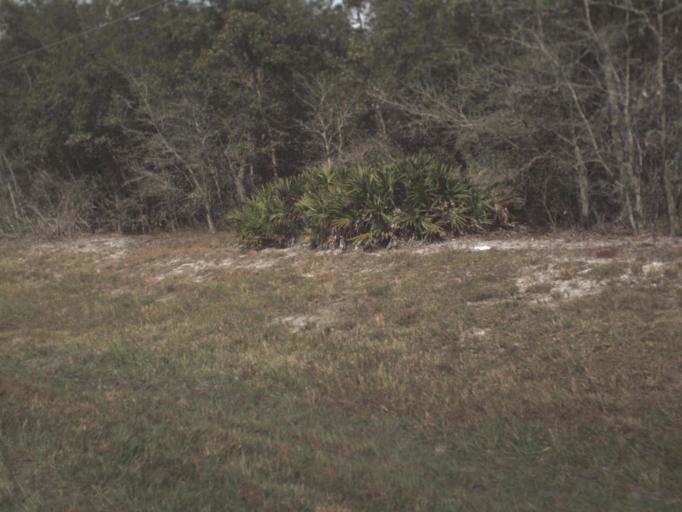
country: US
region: Florida
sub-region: Osceola County
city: Poinciana
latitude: 28.1875
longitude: -81.4630
